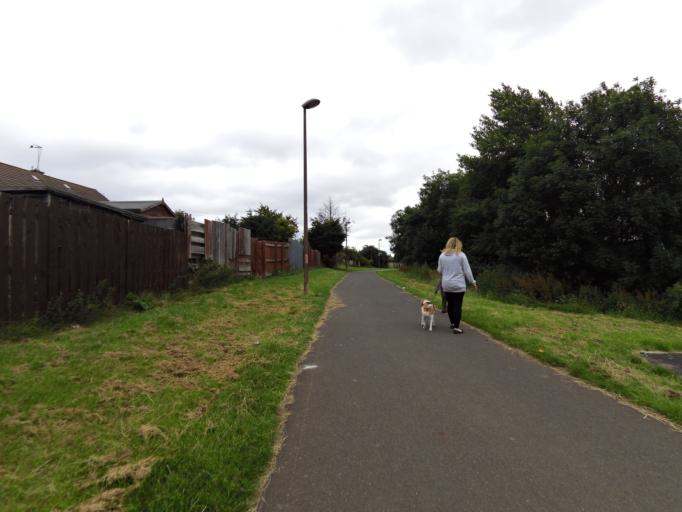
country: GB
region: Scotland
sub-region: West Lothian
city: Seafield
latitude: 55.9406
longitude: -3.1103
